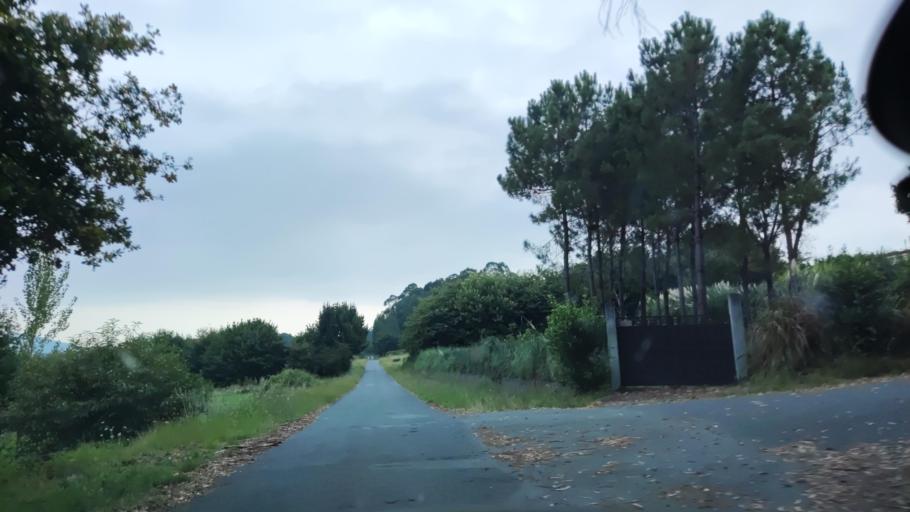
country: ES
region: Galicia
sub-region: Provincia de Pontevedra
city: Catoira
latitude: 42.6982
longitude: -8.7277
